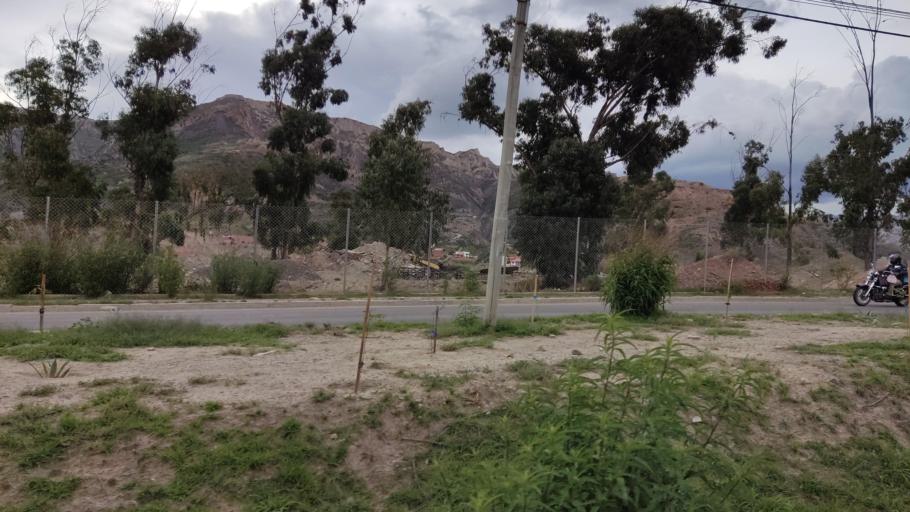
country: BO
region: La Paz
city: La Paz
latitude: -16.5817
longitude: -68.0797
